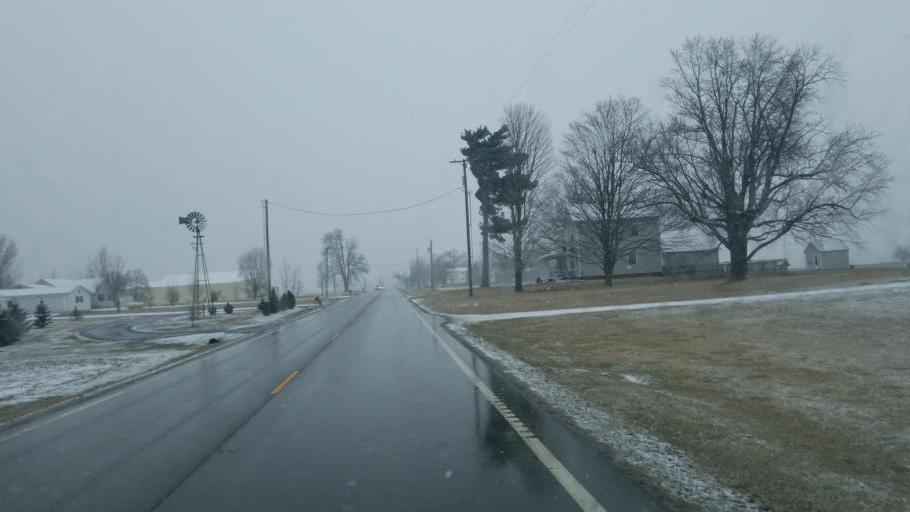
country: US
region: Ohio
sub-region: Defiance County
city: Hicksville
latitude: 41.3121
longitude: -84.7475
